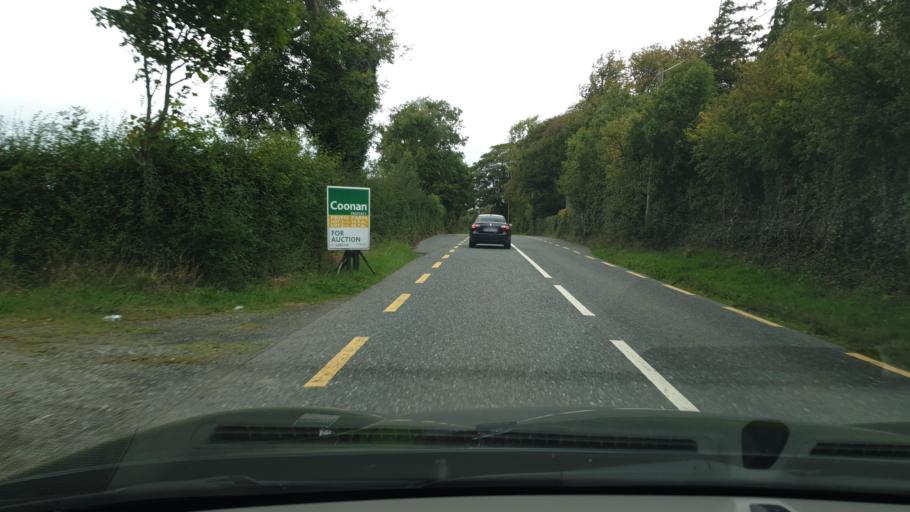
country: IE
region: Leinster
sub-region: Kildare
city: Clane
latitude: 53.2749
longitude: -6.6900
